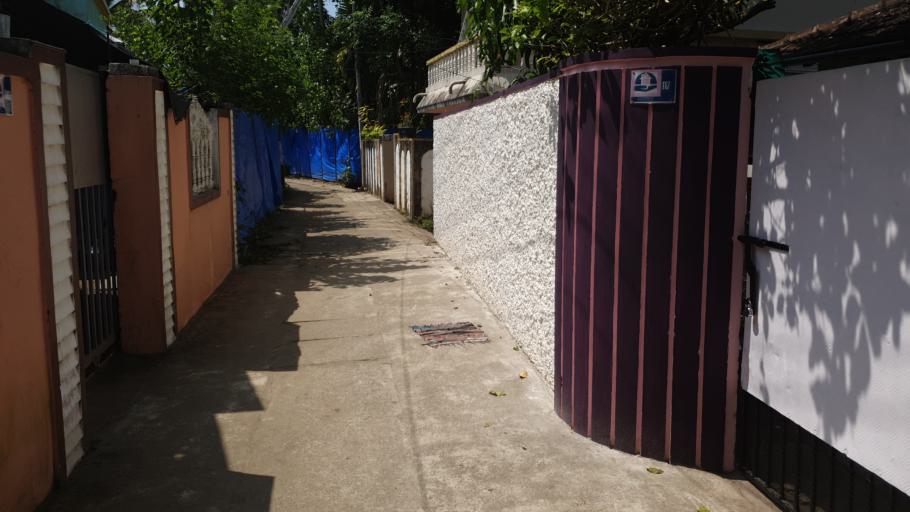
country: IN
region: Kerala
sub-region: Ernakulam
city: Cochin
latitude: 9.9743
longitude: 76.2408
